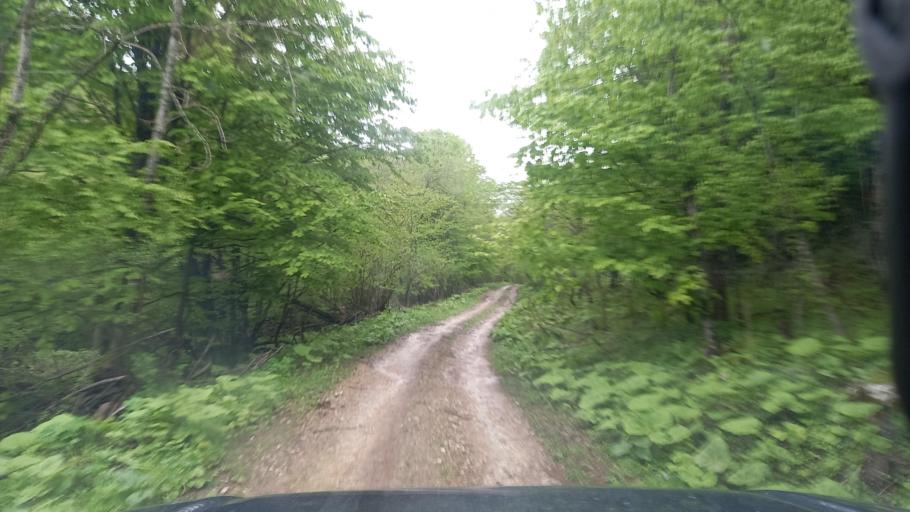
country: RU
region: Kabardino-Balkariya
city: Babugent
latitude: 43.2164
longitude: 43.5501
